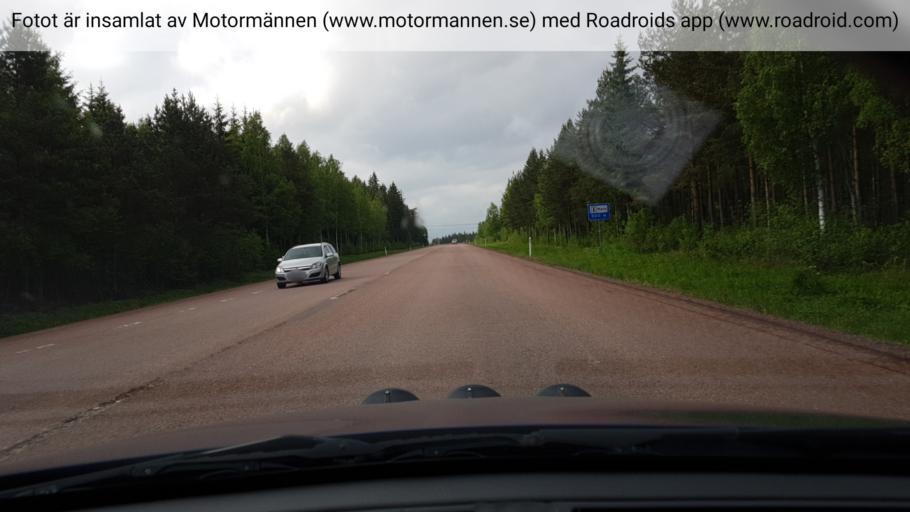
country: SE
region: Dalarna
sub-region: Mora Kommun
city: Mora
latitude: 61.0269
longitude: 14.5900
